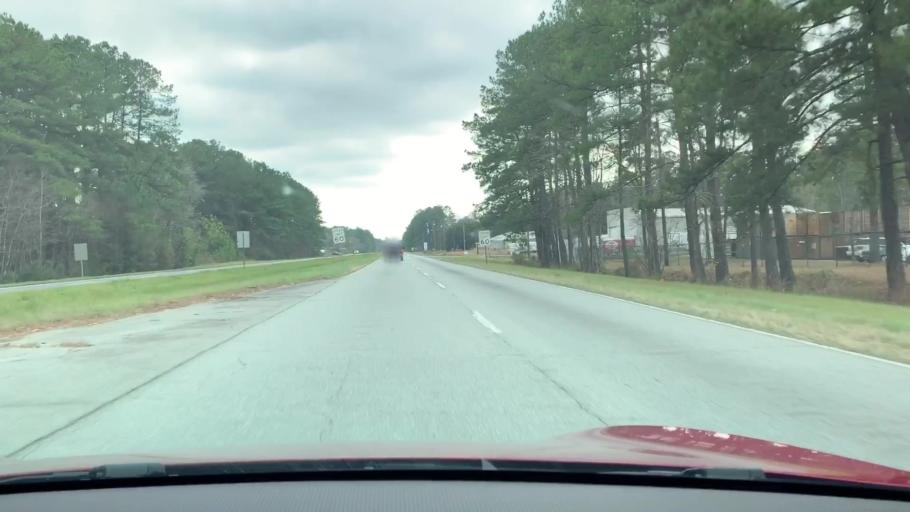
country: US
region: South Carolina
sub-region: Jasper County
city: Hardeeville
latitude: 32.2226
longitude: -81.0736
